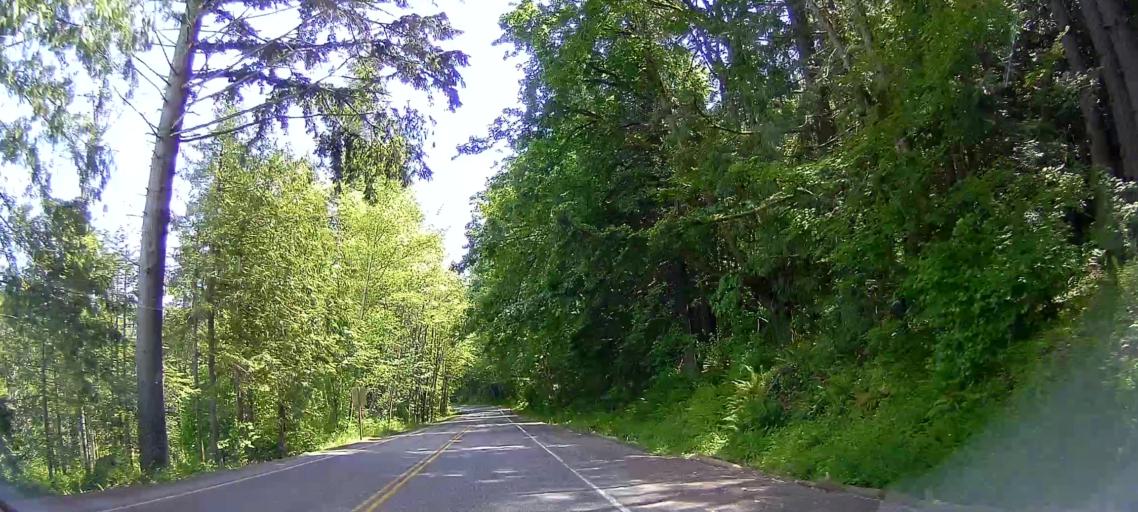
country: US
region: Washington
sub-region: Skagit County
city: Mount Vernon
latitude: 48.3994
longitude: -122.3018
